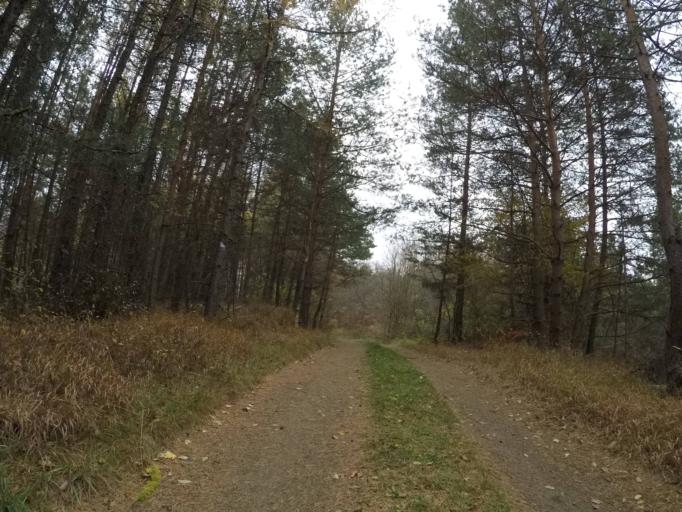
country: SK
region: Presovsky
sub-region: Okres Presov
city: Presov
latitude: 48.8956
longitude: 21.1720
